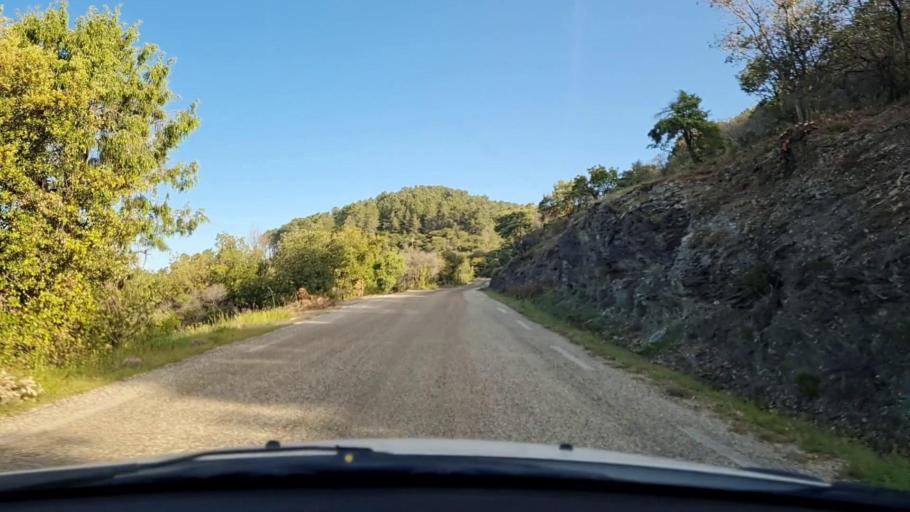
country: FR
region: Languedoc-Roussillon
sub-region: Departement du Gard
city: Branoux-les-Taillades
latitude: 44.1841
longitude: 3.9887
